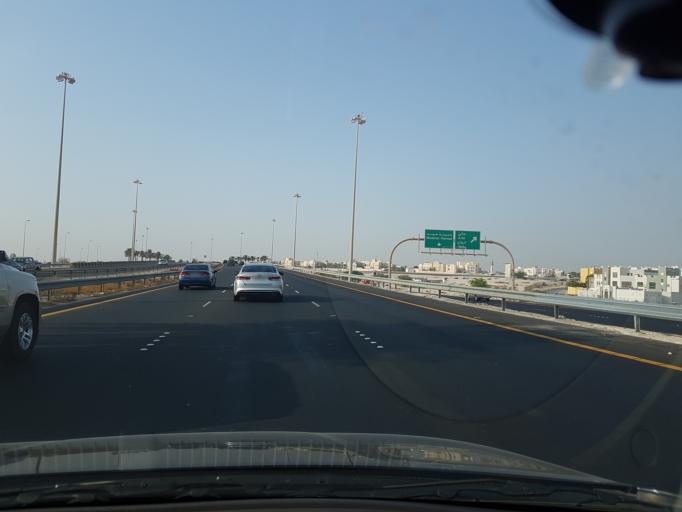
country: BH
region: Central Governorate
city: Madinat Hamad
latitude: 26.1361
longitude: 50.5104
